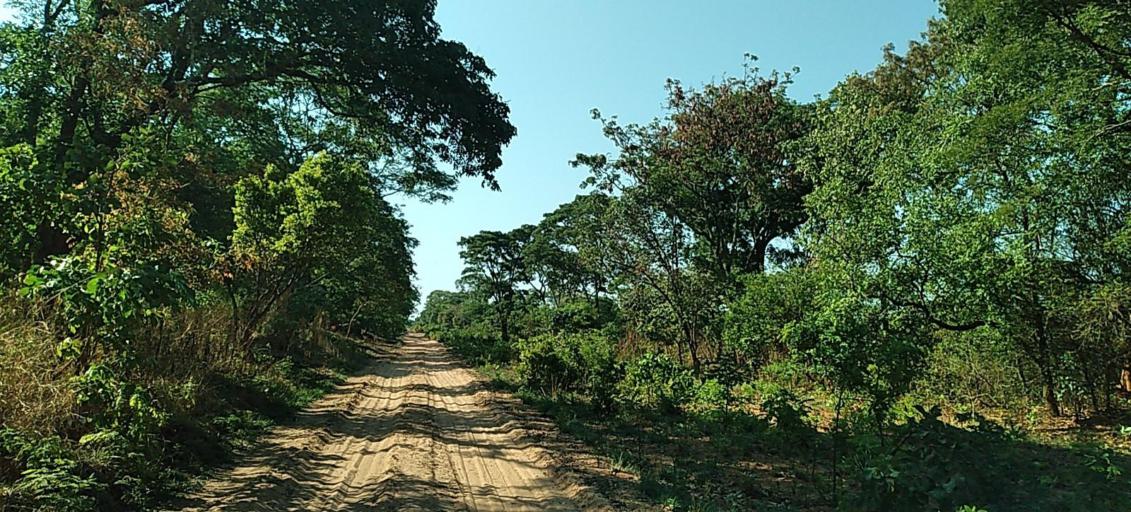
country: ZM
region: Central
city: Mkushi
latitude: -13.4601
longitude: 28.9115
